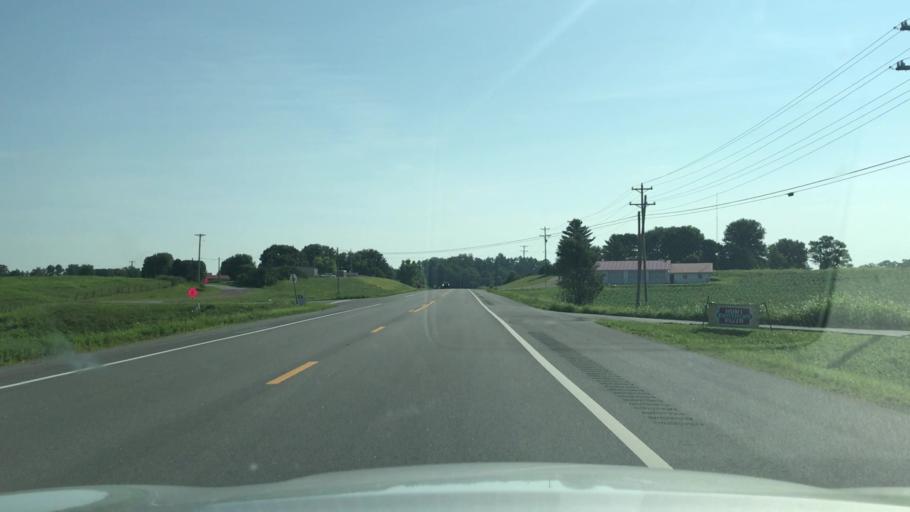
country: US
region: Tennessee
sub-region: Overton County
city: Livingston
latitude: 36.4480
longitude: -85.2154
